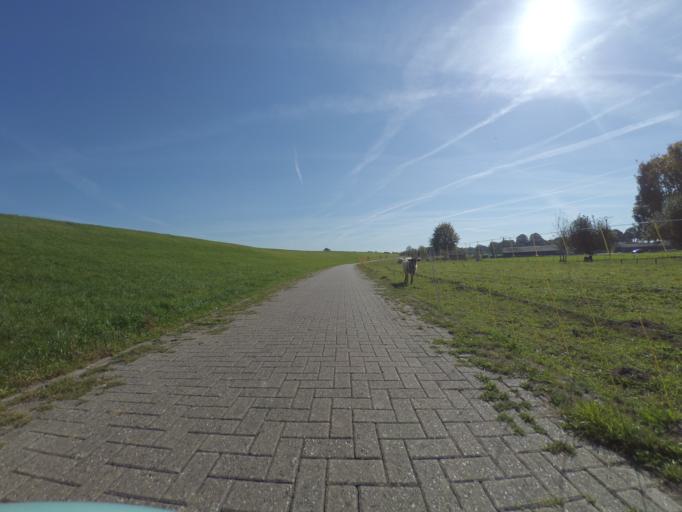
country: NL
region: Gelderland
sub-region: Gemeente Zevenaar
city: Zevenaar
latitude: 51.8577
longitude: 6.0720
